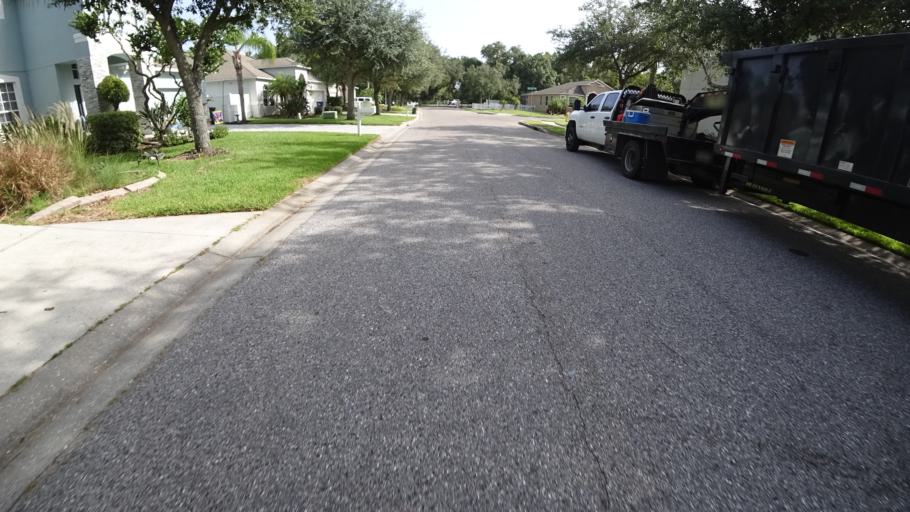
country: US
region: Florida
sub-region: Manatee County
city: Ellenton
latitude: 27.5570
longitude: -82.4970
